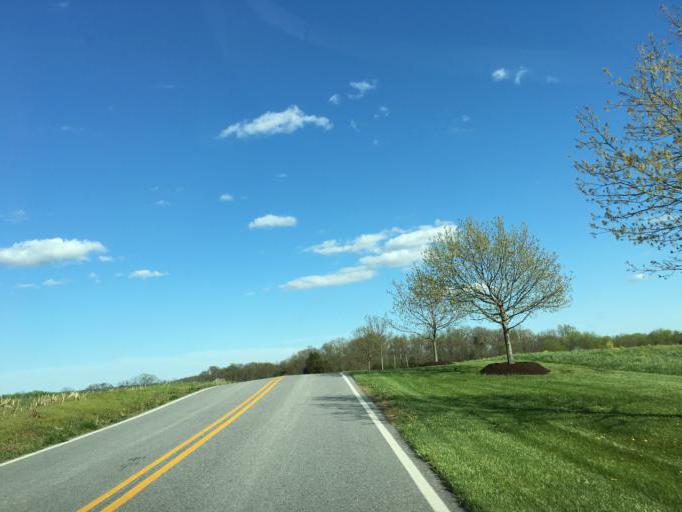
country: US
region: Maryland
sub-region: Frederick County
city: Emmitsburg
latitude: 39.6396
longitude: -77.2939
